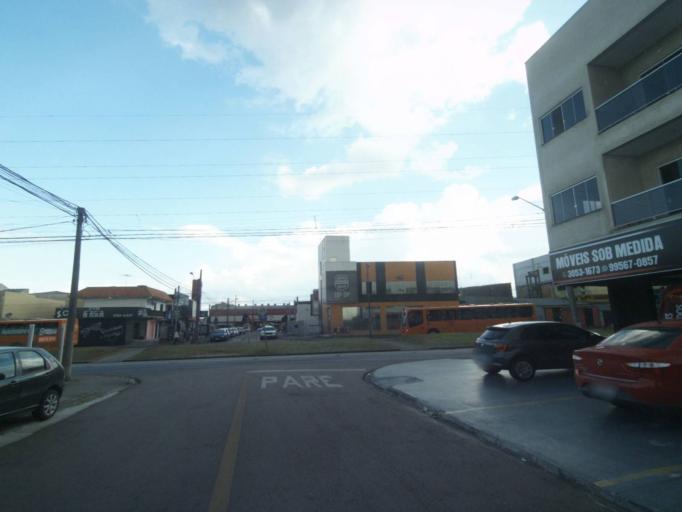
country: BR
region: Parana
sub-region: Sao Jose Dos Pinhais
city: Sao Jose dos Pinhais
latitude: -25.5346
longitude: -49.2710
